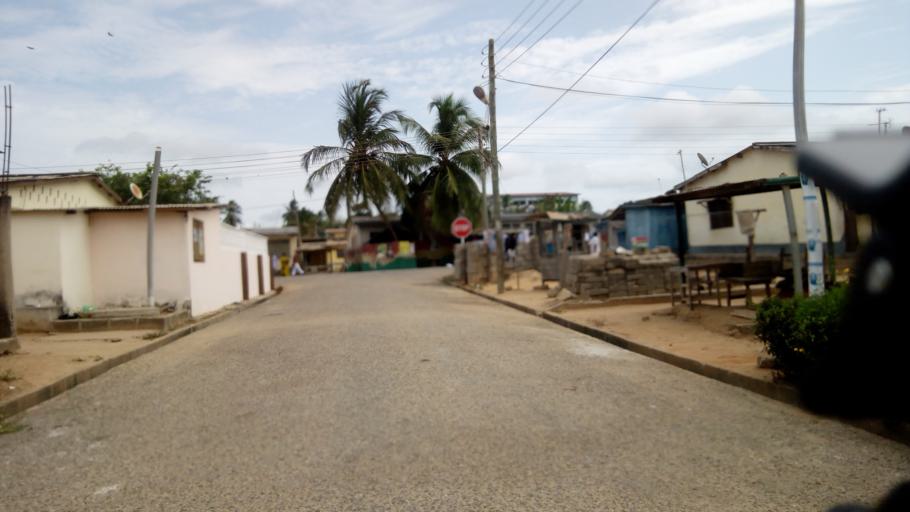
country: GH
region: Central
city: Cape Coast
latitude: 5.1020
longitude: -1.2773
